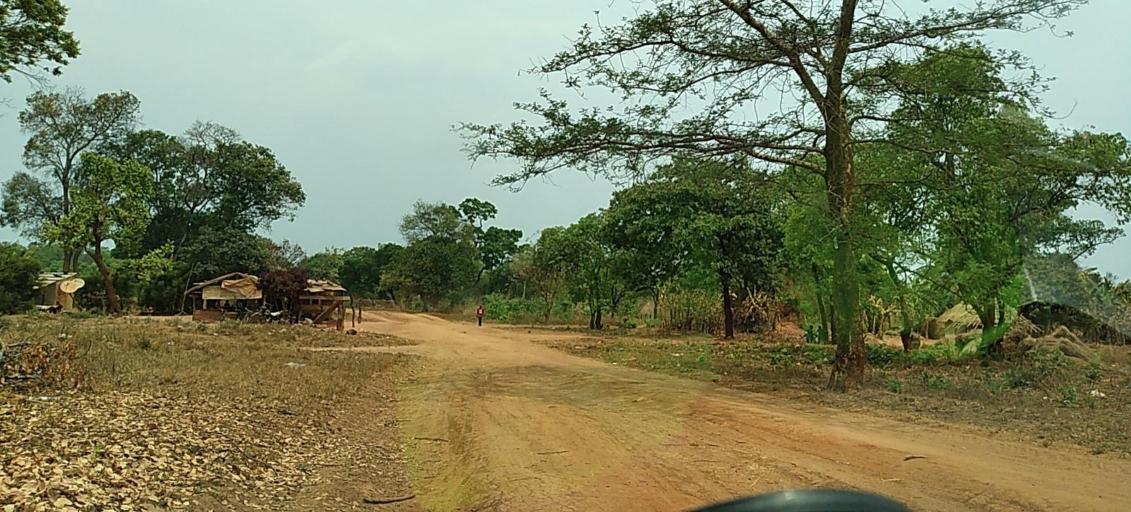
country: ZM
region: North-Western
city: Solwezi
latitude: -12.8003
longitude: 26.5351
